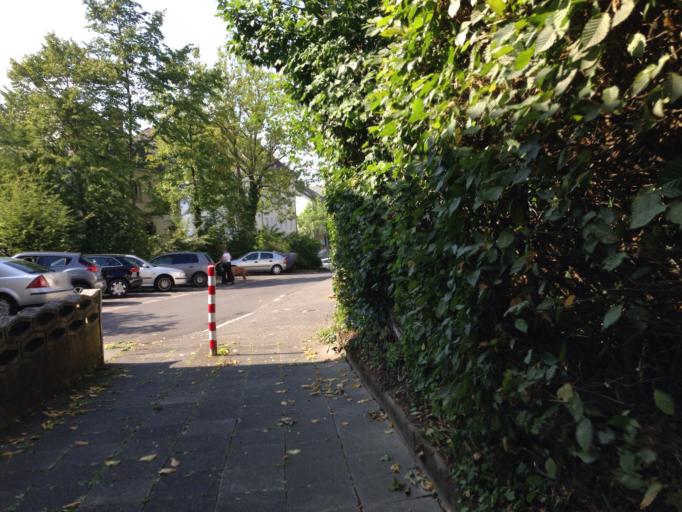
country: DE
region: Hesse
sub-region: Regierungsbezirk Giessen
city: Giessen
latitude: 50.5800
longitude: 8.6836
